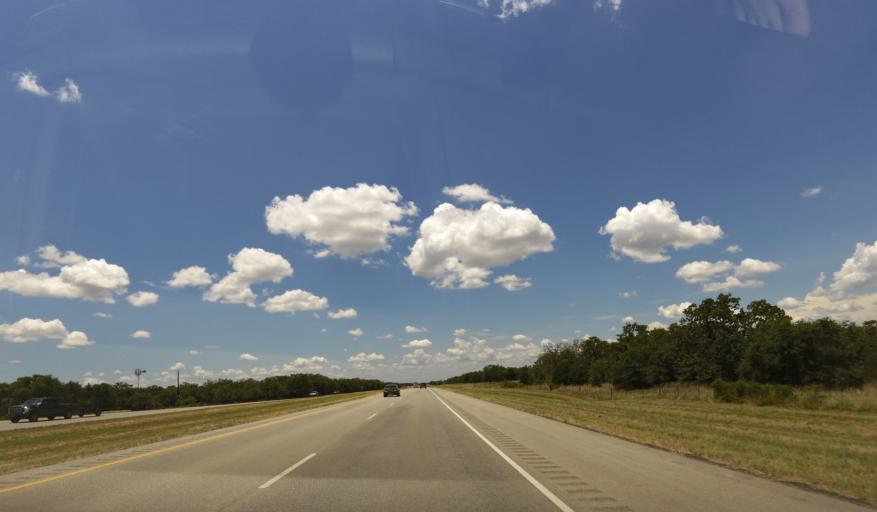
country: US
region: Texas
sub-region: Lee County
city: Giddings
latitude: 30.1413
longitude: -96.7669
